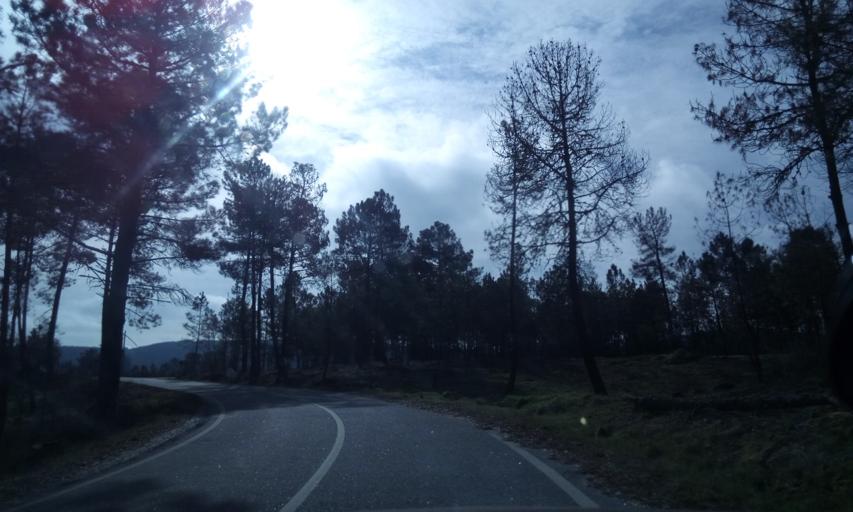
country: PT
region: Guarda
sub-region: Fornos de Algodres
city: Fornos de Algodres
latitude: 40.7046
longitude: -7.5646
